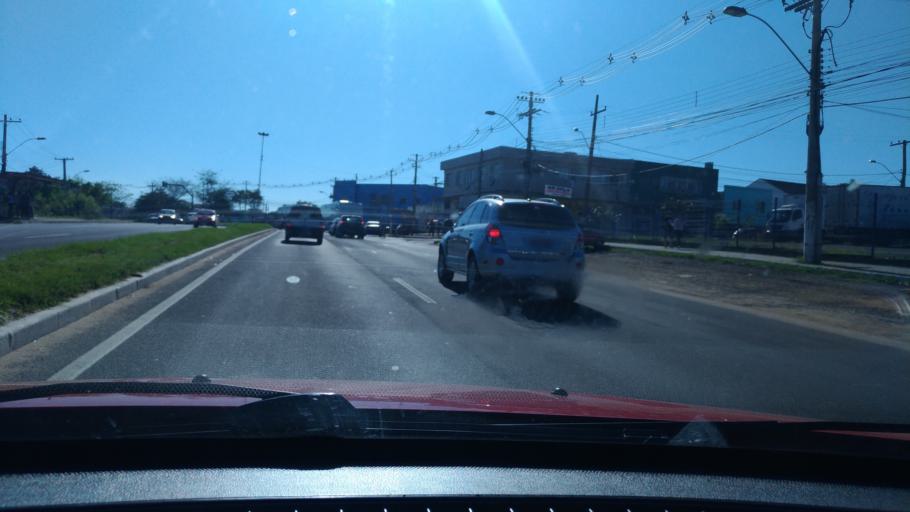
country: BR
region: Rio Grande do Sul
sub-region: Viamao
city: Viamao
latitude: -30.0926
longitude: -51.0652
